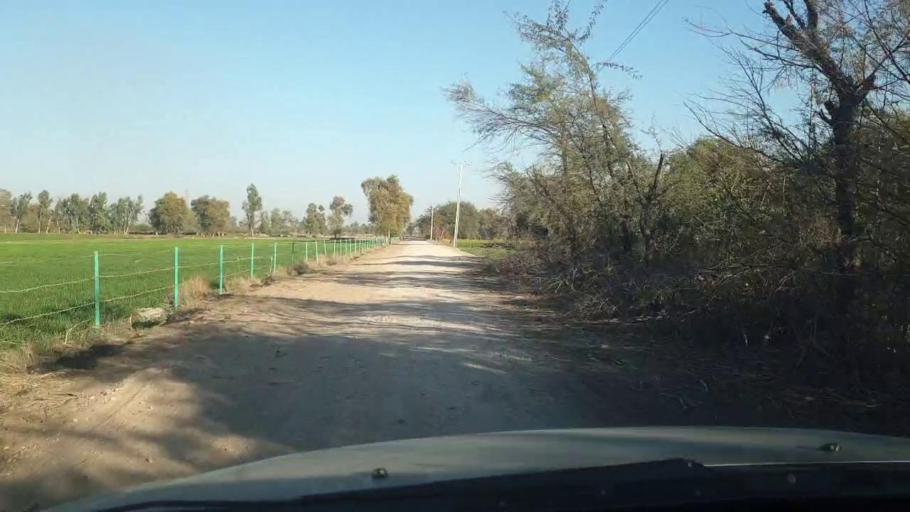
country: PK
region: Sindh
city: Ghotki
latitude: 28.0386
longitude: 69.3213
